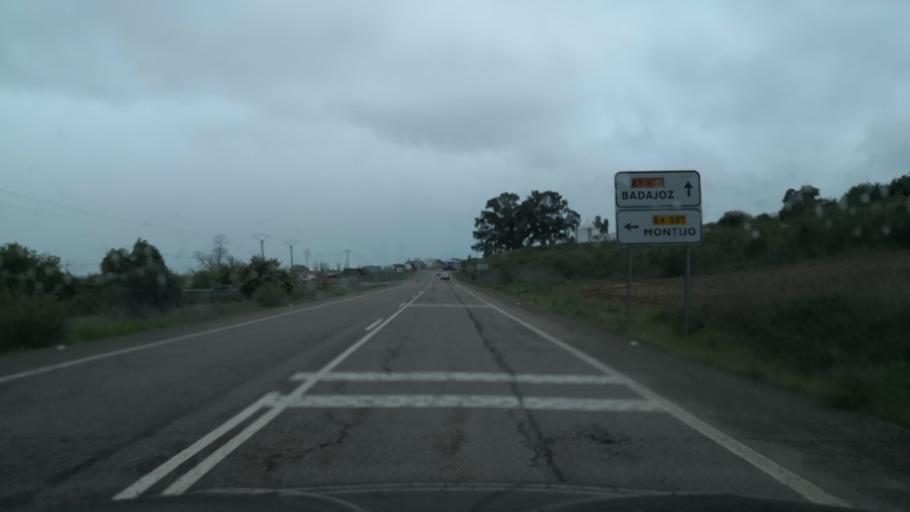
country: ES
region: Extremadura
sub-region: Provincia de Badajoz
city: La Roca de la Sierra
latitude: 39.1152
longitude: -6.6857
